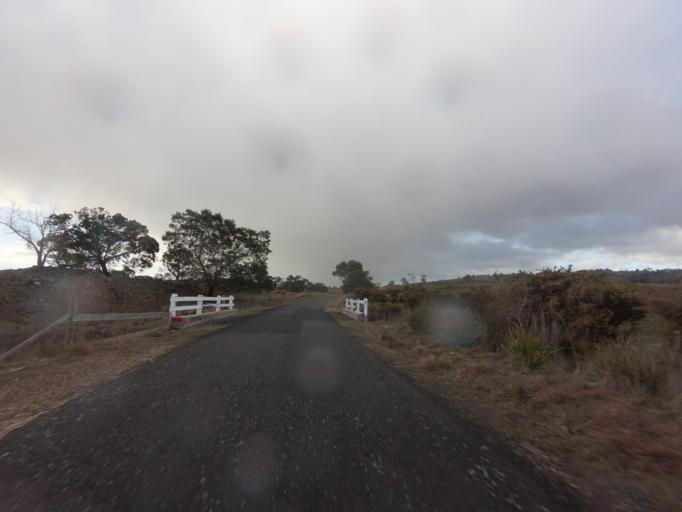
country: AU
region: Tasmania
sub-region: Break O'Day
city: St Helens
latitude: -41.9997
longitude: 148.0888
